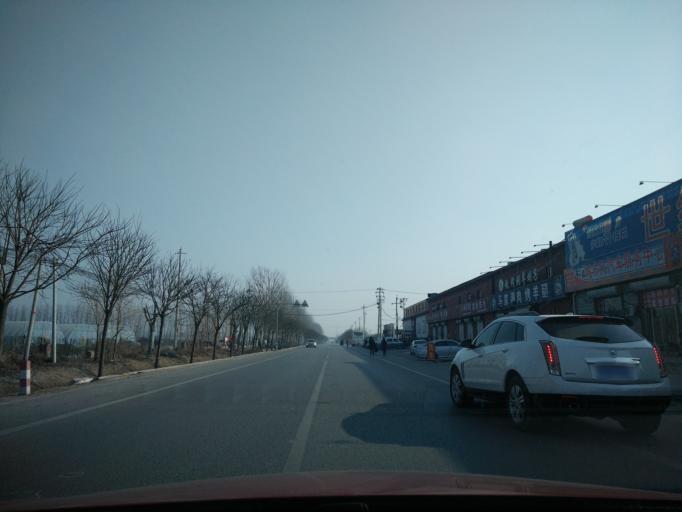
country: CN
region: Beijing
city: Yinghai
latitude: 39.7053
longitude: 116.4347
